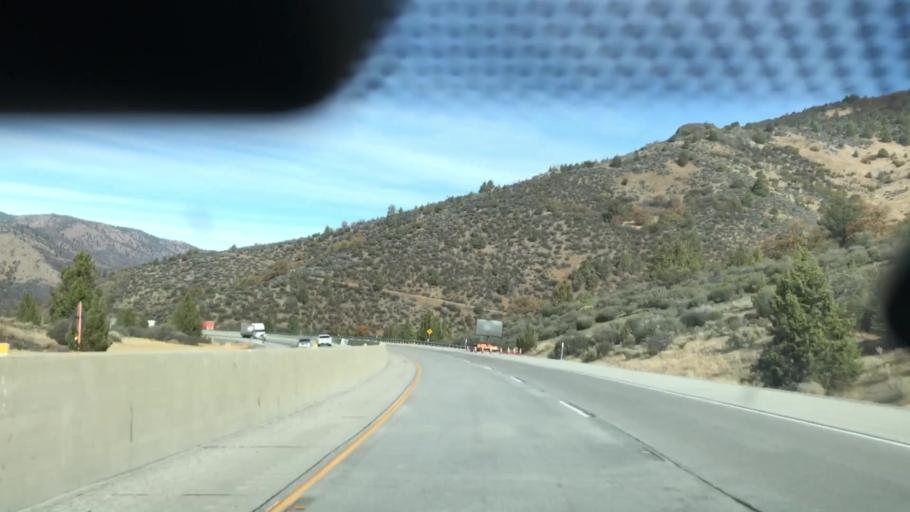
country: US
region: California
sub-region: Siskiyou County
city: Montague
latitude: 41.8106
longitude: -122.5719
